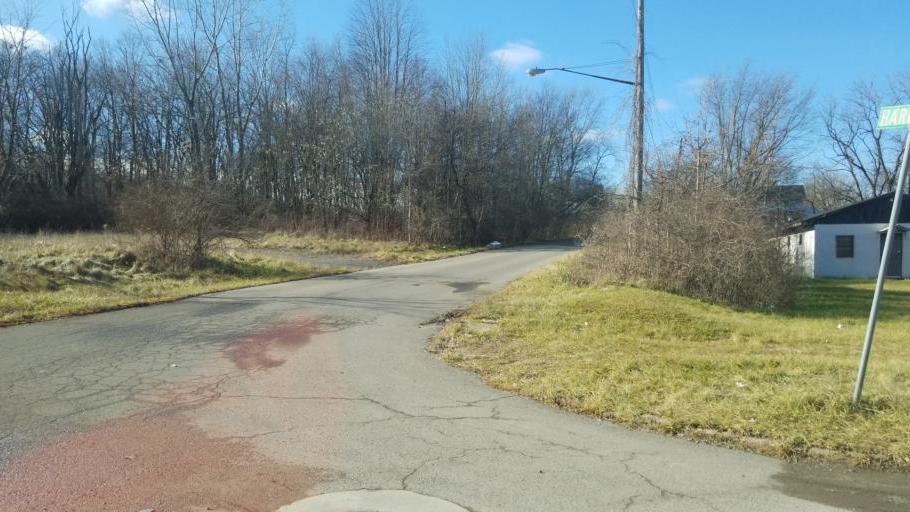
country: US
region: Ohio
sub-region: Richland County
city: Mansfield
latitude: 40.7871
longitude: -82.5257
